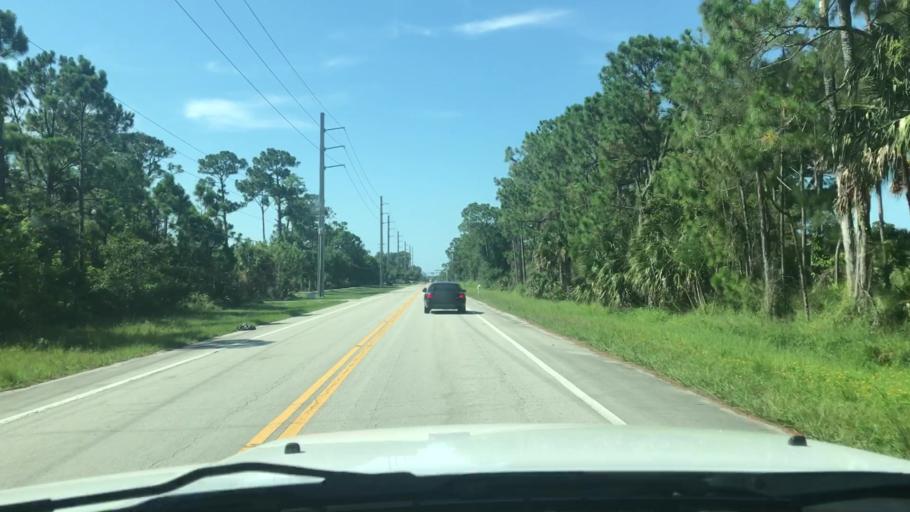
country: US
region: Florida
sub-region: Indian River County
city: Winter Beach
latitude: 27.7284
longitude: -80.4458
